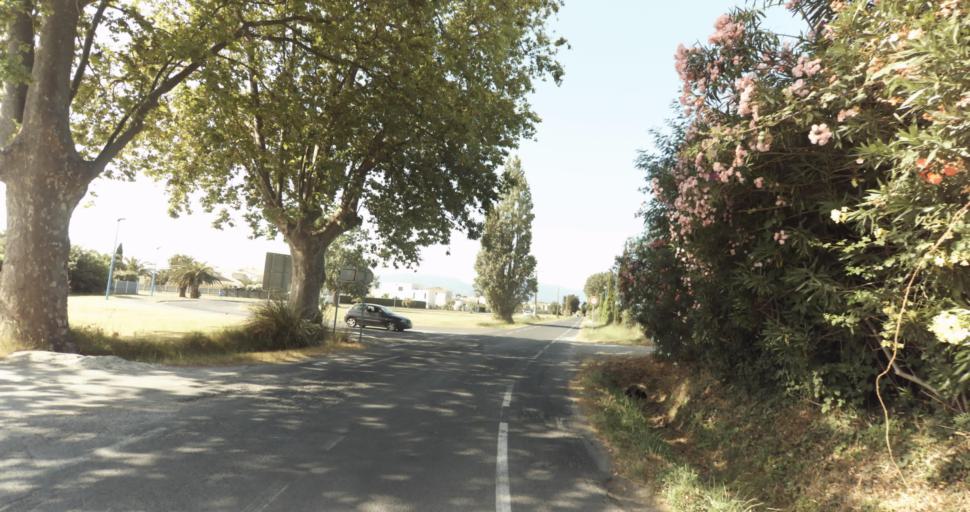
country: FR
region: Languedoc-Roussillon
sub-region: Departement des Pyrenees-Orientales
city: Latour-Bas-Elne
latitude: 42.6259
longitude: 3.0028
